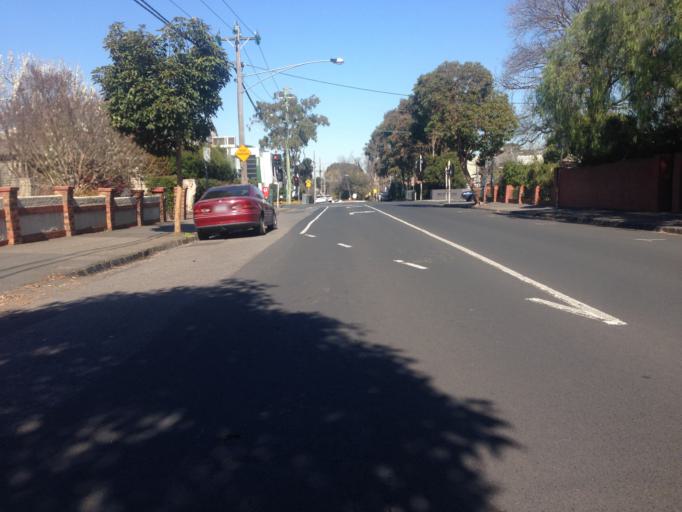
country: AU
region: Victoria
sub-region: Boroondara
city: Kew
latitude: -37.8090
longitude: 145.0351
